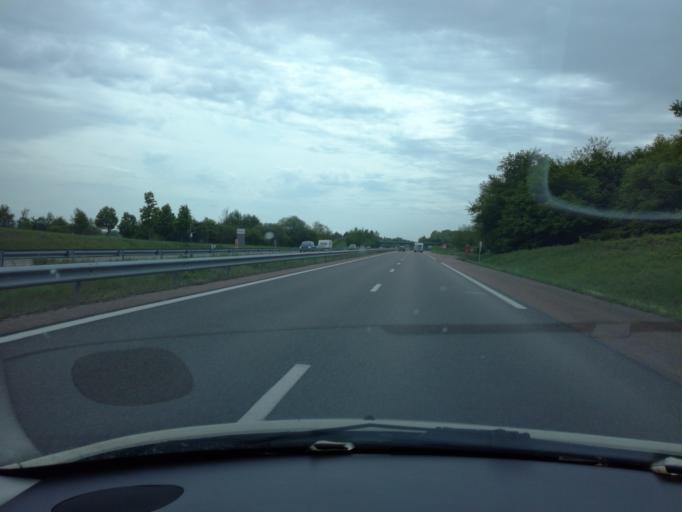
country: FR
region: Franche-Comte
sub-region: Departement du Jura
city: Mont-sous-Vaudrey
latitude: 46.8711
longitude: 5.5815
